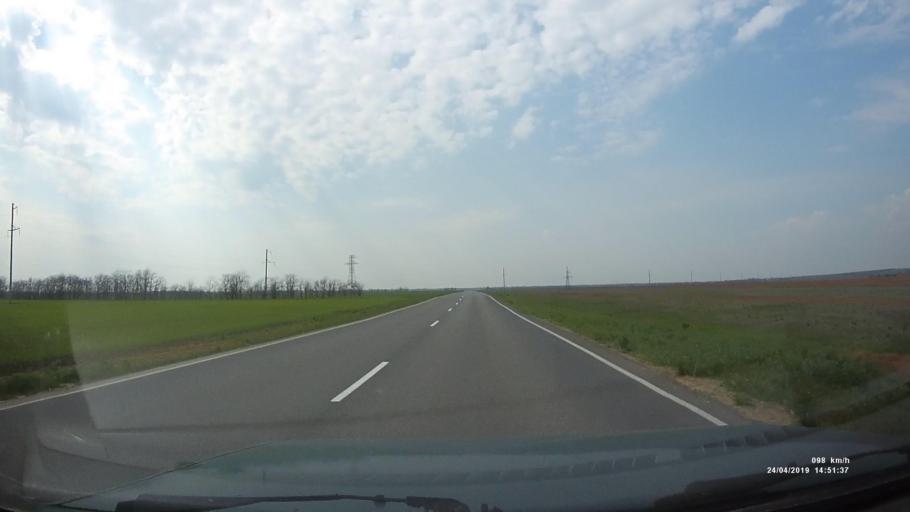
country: RU
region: Rostov
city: Remontnoye
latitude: 46.5262
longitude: 43.6972
